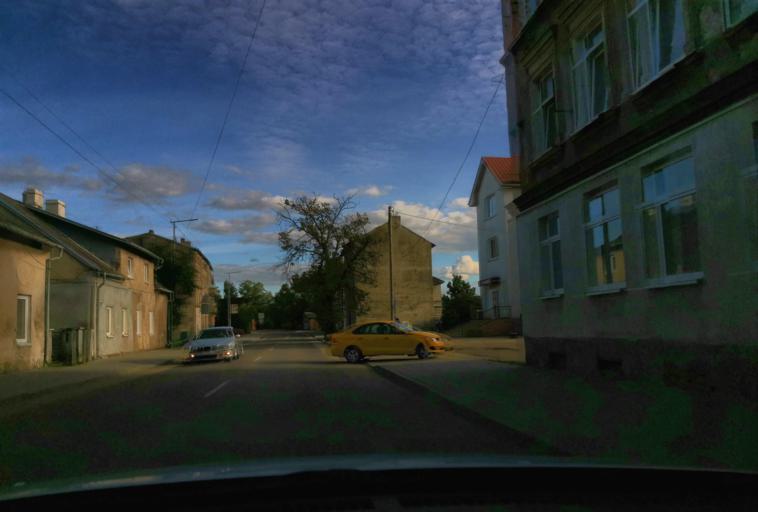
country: RU
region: Kaliningrad
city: Chernyakhovsk
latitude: 54.6269
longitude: 21.8132
